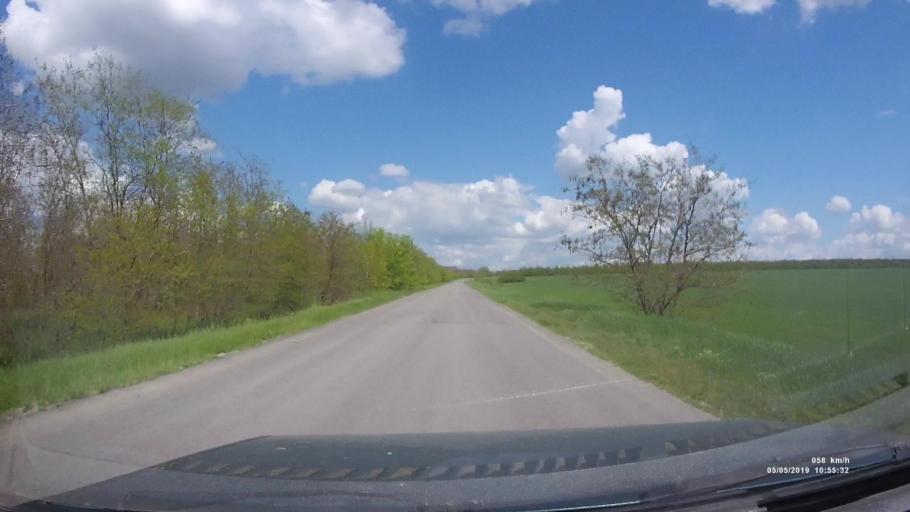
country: RU
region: Rostov
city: Ust'-Donetskiy
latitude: 47.6664
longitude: 40.8208
